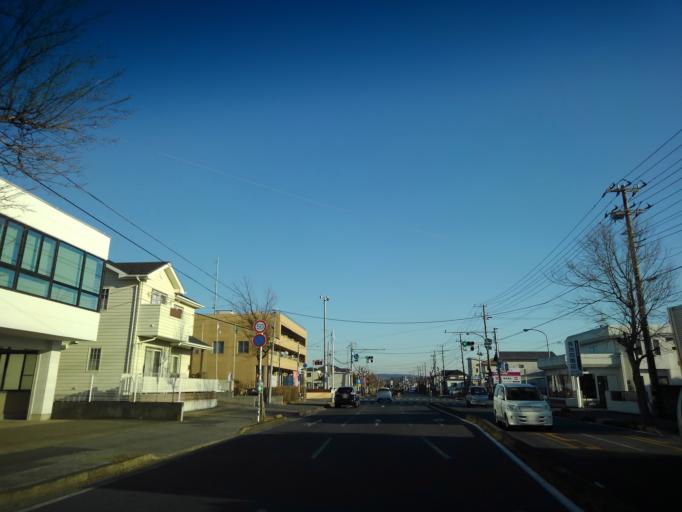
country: JP
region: Chiba
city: Kimitsu
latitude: 35.3218
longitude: 139.9124
